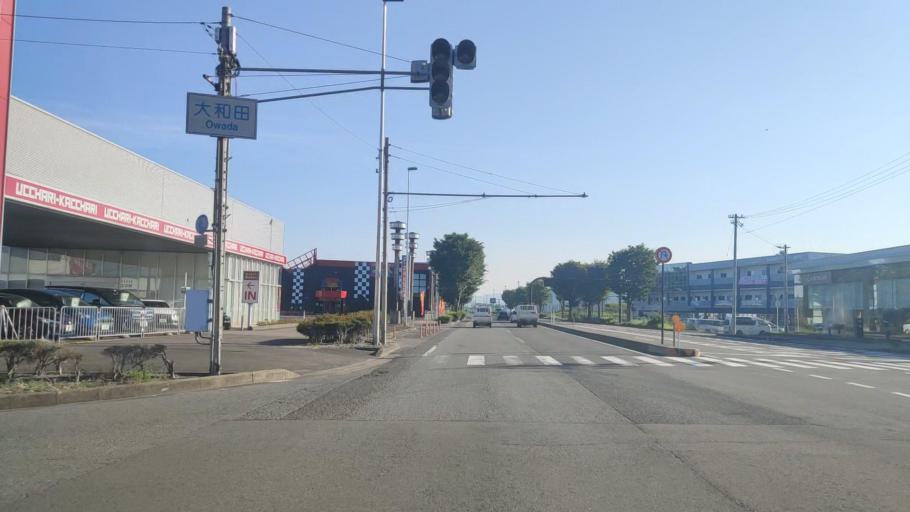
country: JP
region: Fukui
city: Fukui-shi
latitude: 36.0979
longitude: 136.2526
